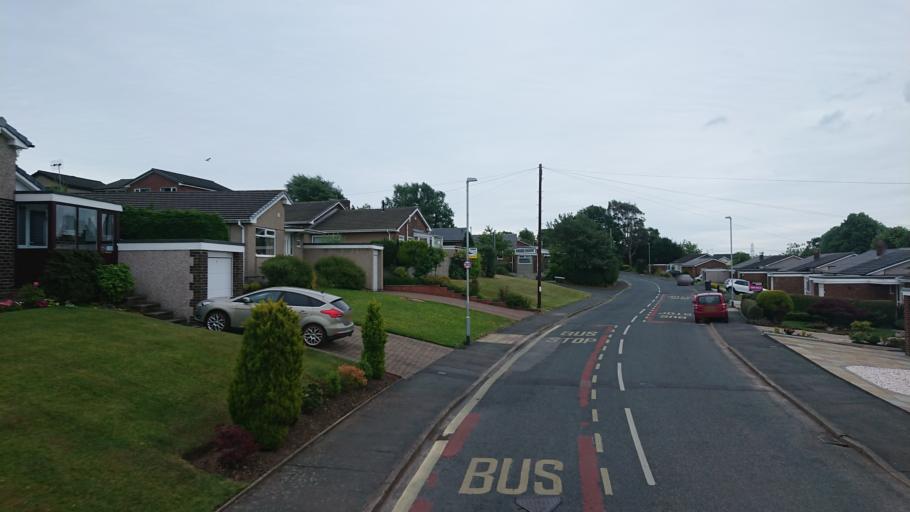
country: GB
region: England
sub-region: Lancashire
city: Lancaster
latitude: 54.0294
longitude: -2.7858
